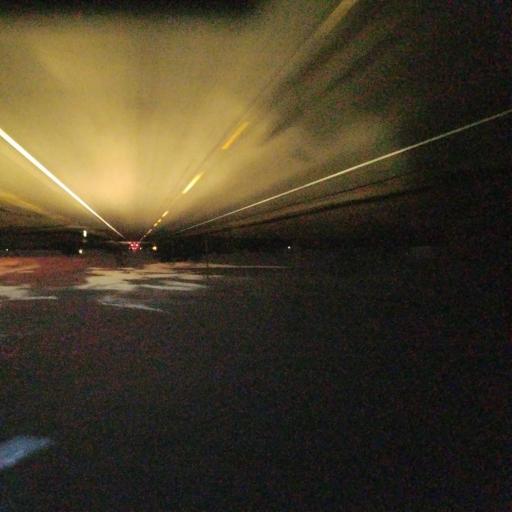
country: US
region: Illinois
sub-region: Fulton County
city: Farmington
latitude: 40.6982
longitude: -89.9396
